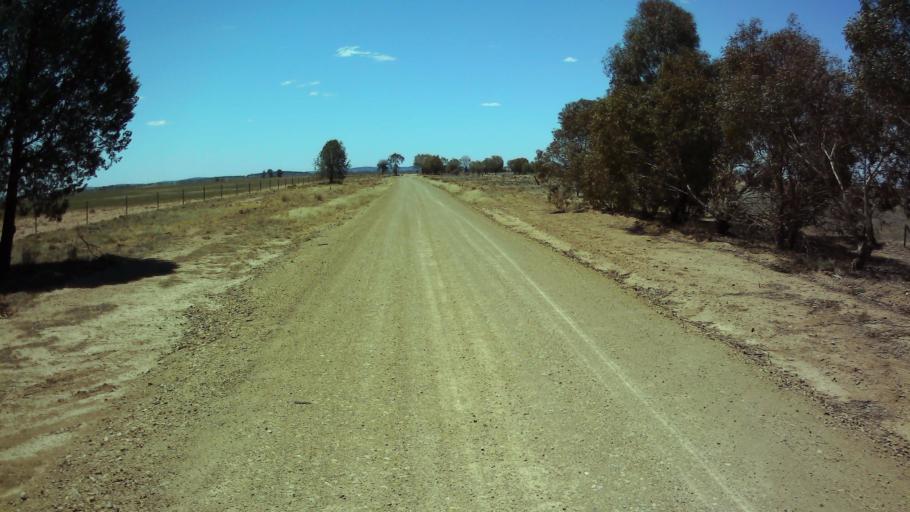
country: AU
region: New South Wales
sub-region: Weddin
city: Grenfell
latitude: -33.8388
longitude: 147.7415
